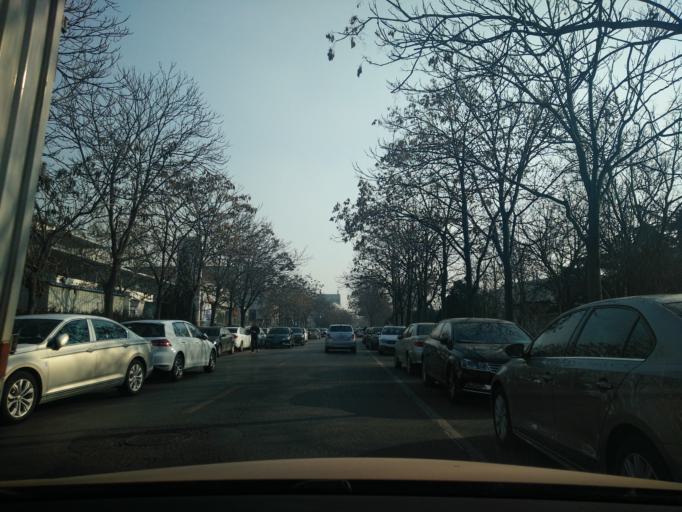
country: CN
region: Beijing
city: Jiugong
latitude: 39.8087
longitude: 116.5057
